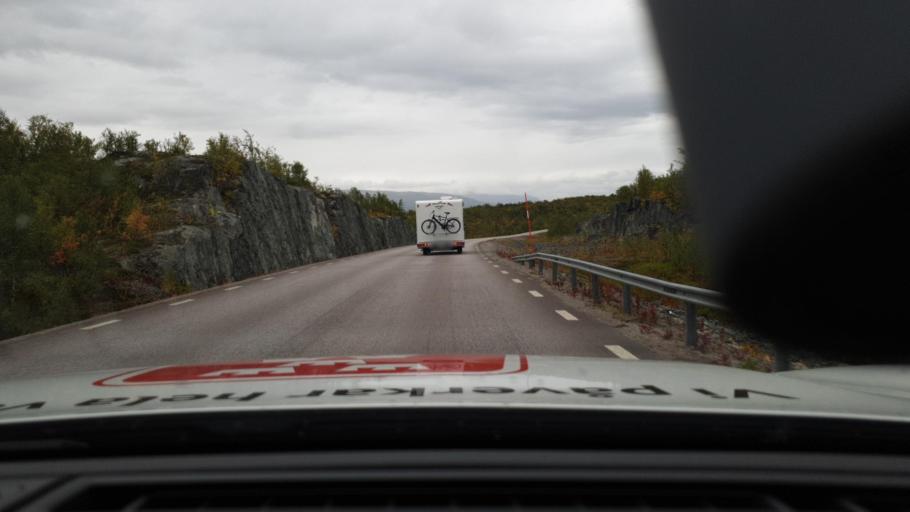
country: NO
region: Troms
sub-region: Bardu
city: Setermoen
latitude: 68.4430
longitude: 18.6177
